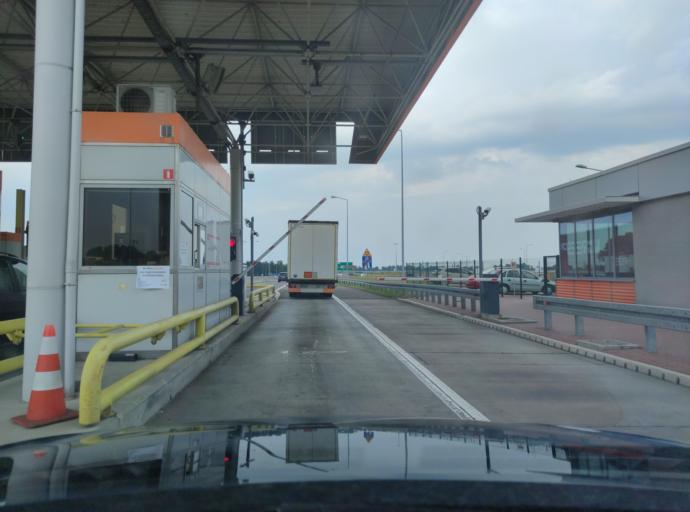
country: PL
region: Opole Voivodeship
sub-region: Powiat strzelecki
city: Strzelce Opolskie
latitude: 50.4621
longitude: 18.2727
